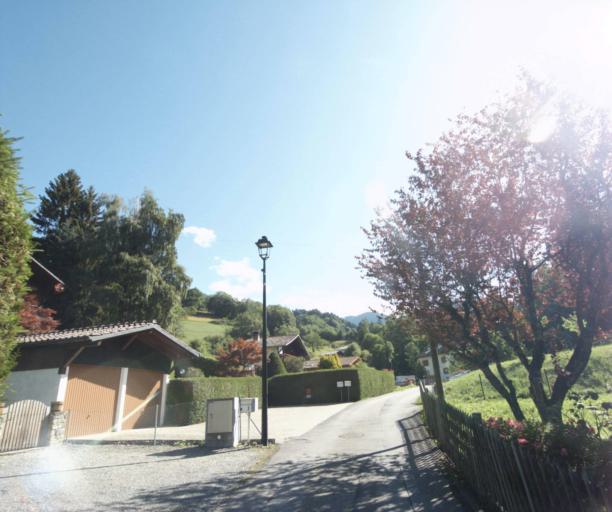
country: CH
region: Vaud
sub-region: Aigle District
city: Villars-sur-Ollon
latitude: 46.2874
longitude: 7.0280
